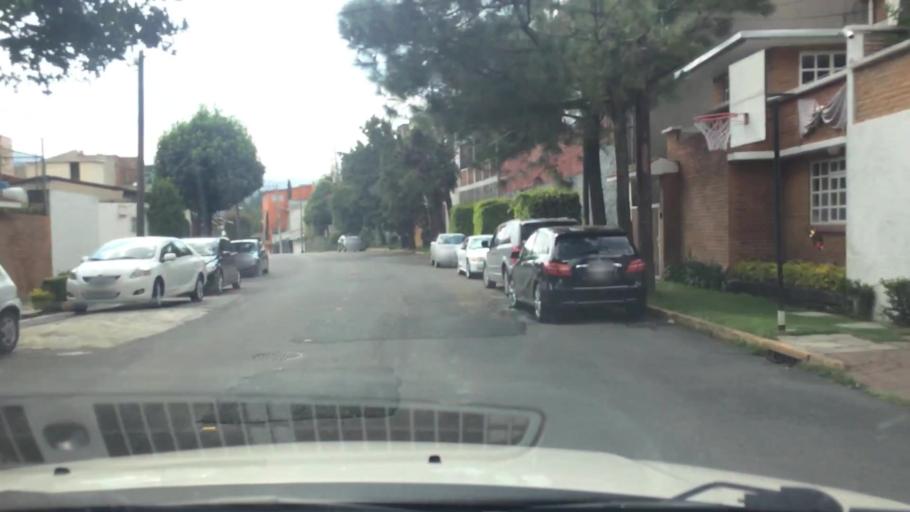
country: MX
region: Mexico City
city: Magdalena Contreras
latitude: 19.3426
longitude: -99.2412
